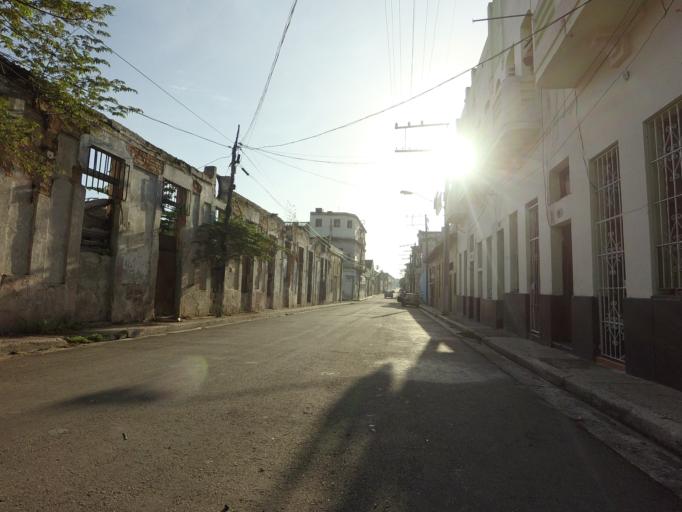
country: CU
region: La Habana
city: Havana
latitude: 23.1266
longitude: -82.3736
